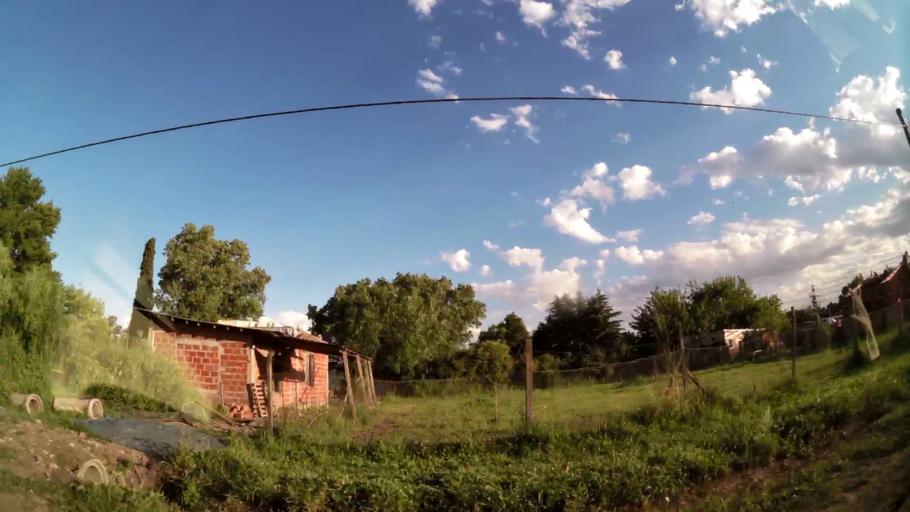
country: AR
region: Buenos Aires
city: Santa Catalina - Dique Lujan
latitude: -34.4729
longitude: -58.7488
